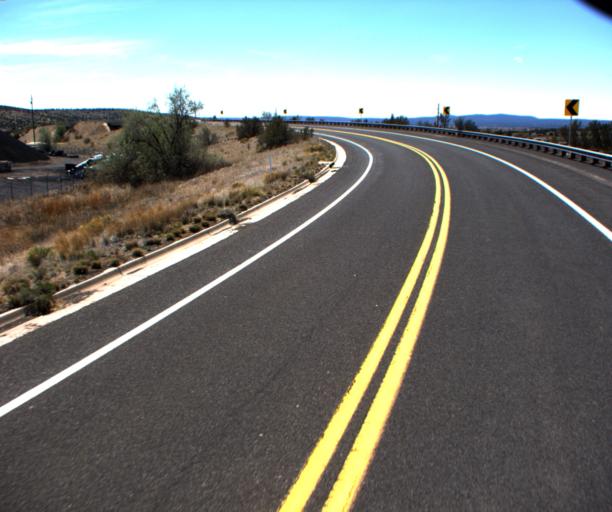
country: US
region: Arizona
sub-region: Mohave County
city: Peach Springs
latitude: 35.3313
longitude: -112.8891
